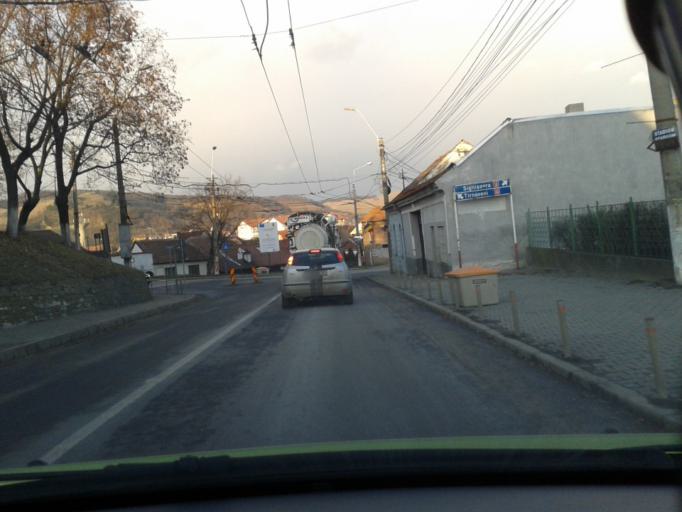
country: RO
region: Sibiu
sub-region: Municipiul Medias
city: Medias
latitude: 46.1645
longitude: 24.3563
